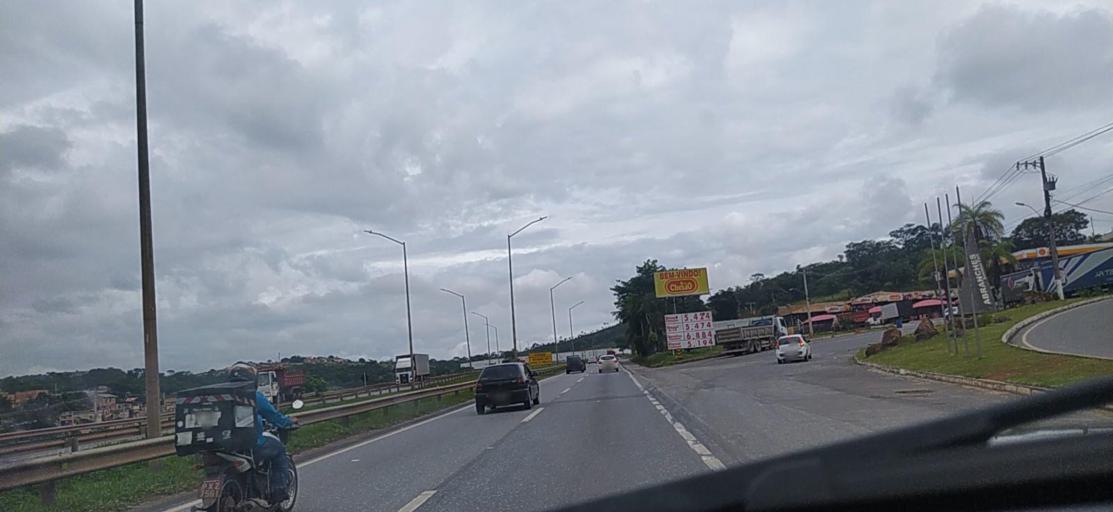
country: BR
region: Minas Gerais
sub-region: Ribeirao Das Neves
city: Ribeirao das Neves
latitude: -19.7514
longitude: -44.1440
